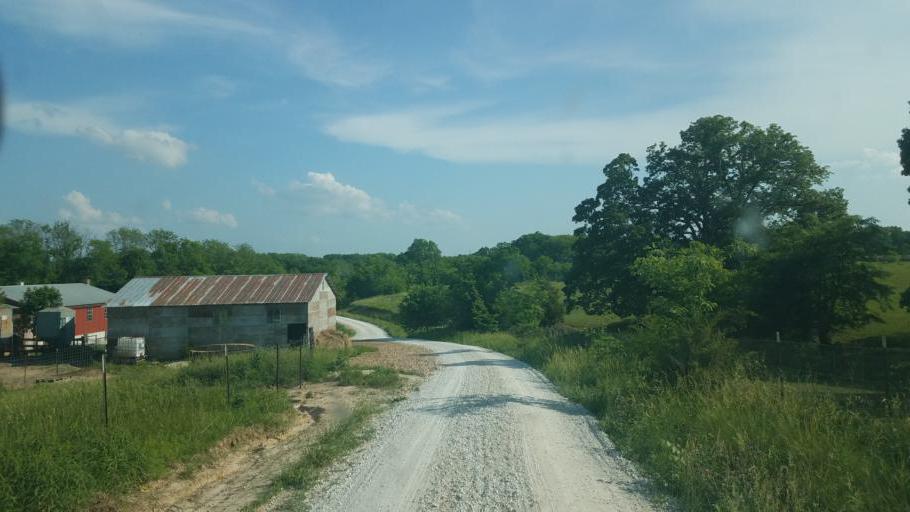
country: US
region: Missouri
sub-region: Cooper County
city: Boonville
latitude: 38.8538
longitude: -92.6460
